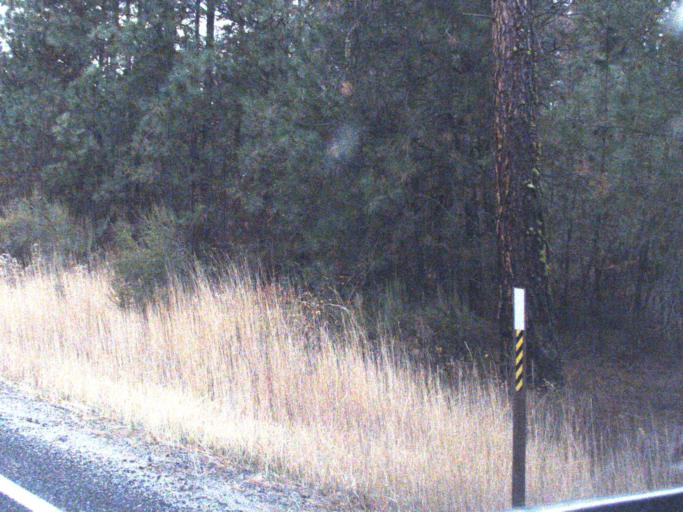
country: US
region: Washington
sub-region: Lincoln County
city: Davenport
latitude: 48.0240
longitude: -118.2354
